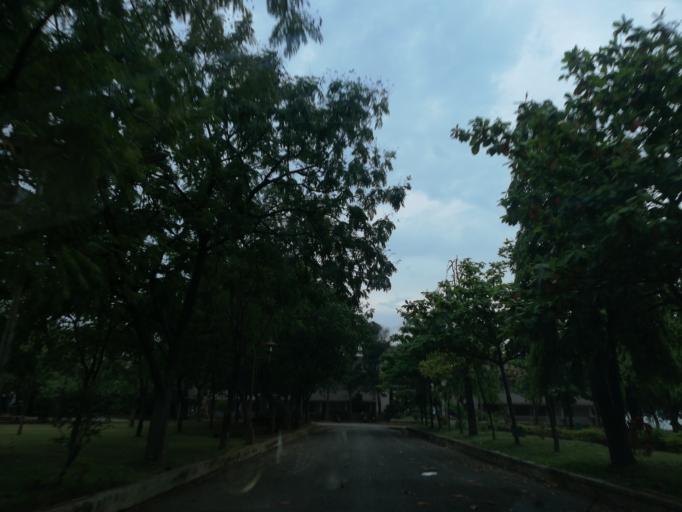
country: IN
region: Andhra Pradesh
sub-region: Guntur
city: Macherla
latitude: 16.6112
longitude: 79.2957
